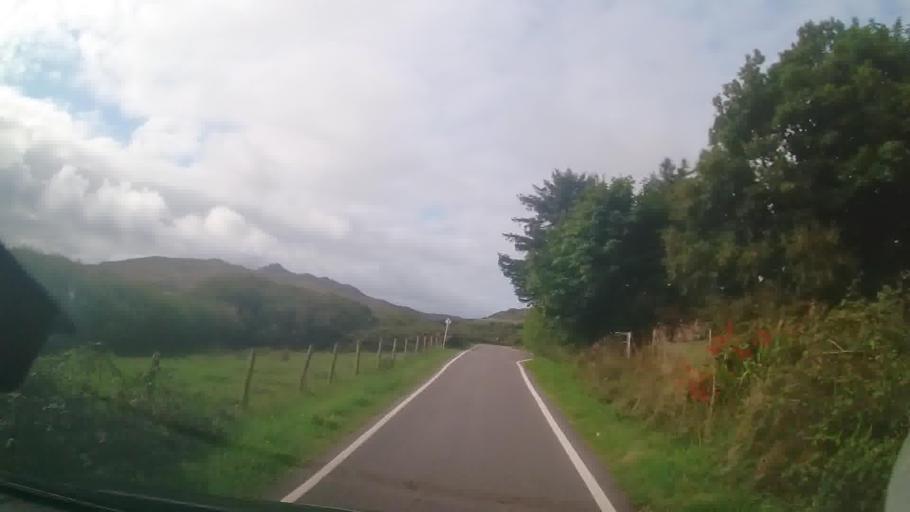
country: GB
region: Scotland
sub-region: Argyll and Bute
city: Isle Of Mull
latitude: 56.6949
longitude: -6.0982
